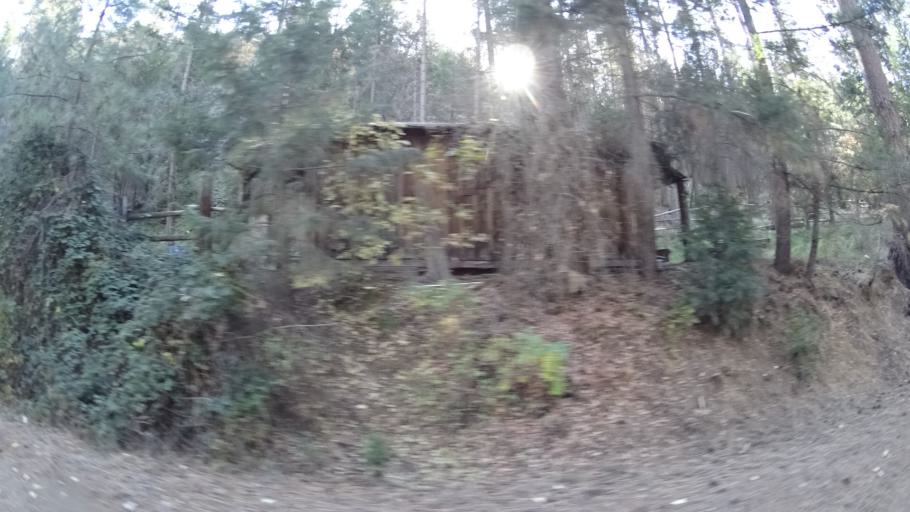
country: US
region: California
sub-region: Siskiyou County
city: Yreka
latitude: 41.8318
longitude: -122.9489
